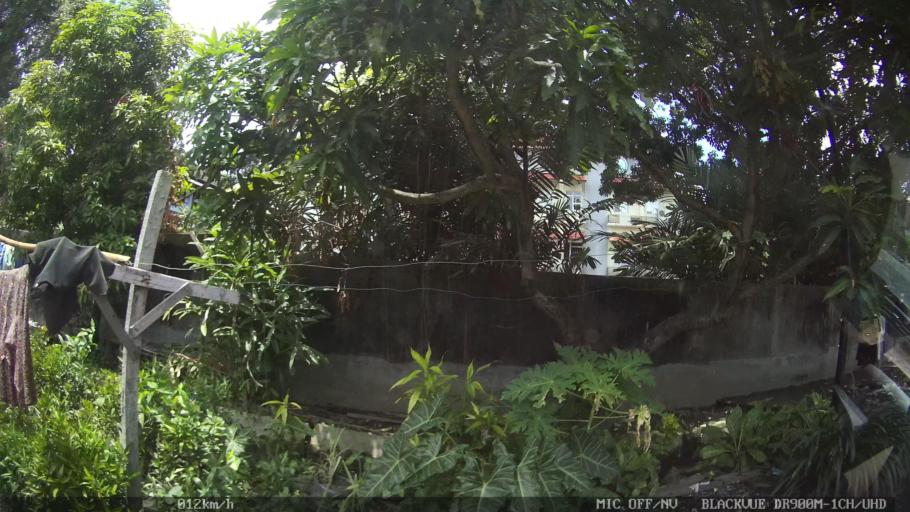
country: ID
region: North Sumatra
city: Medan
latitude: 3.6071
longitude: 98.7221
